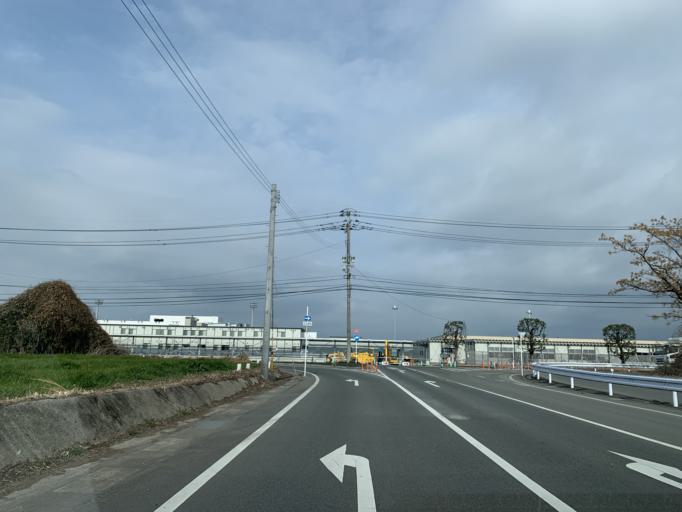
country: JP
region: Kumamoto
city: Ozu
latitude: 32.8340
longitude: 130.8626
